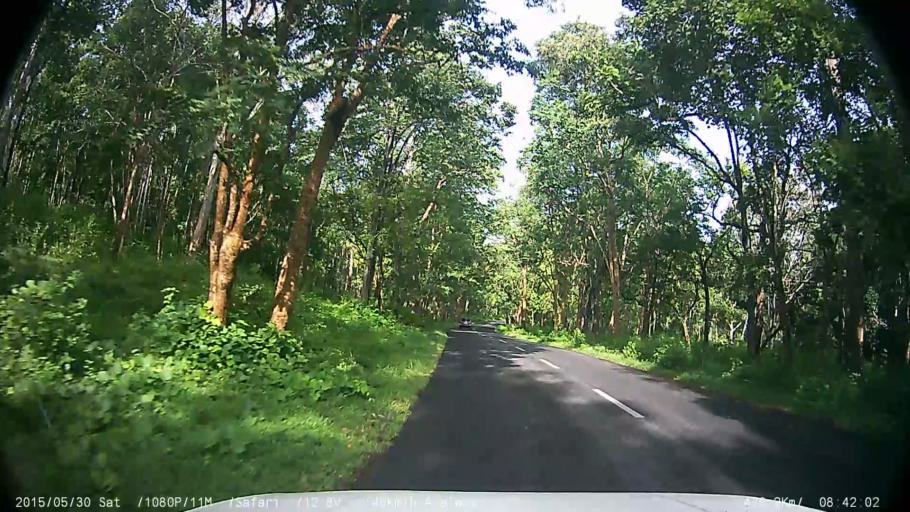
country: IN
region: Tamil Nadu
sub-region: Nilgiri
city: Naduvattam
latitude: 11.7052
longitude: 76.4066
